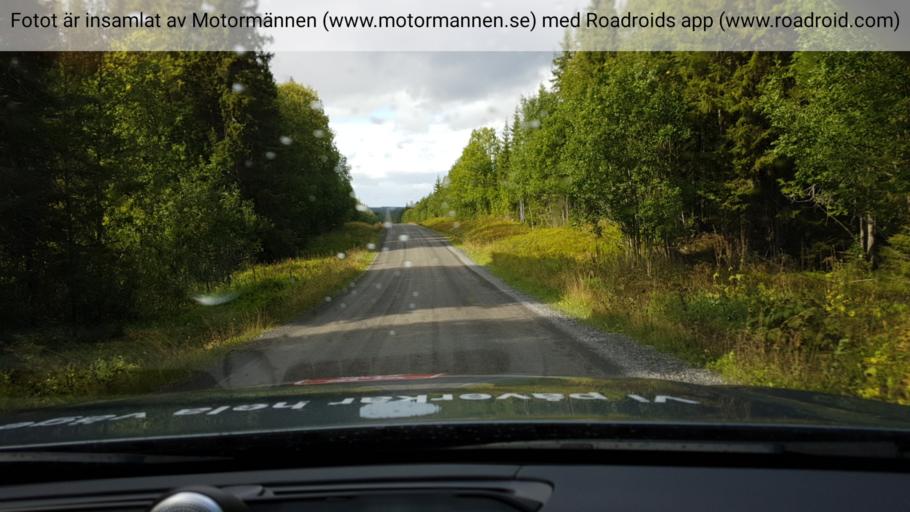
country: SE
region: Jaemtland
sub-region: OEstersunds Kommun
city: Lit
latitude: 63.6472
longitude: 14.9498
